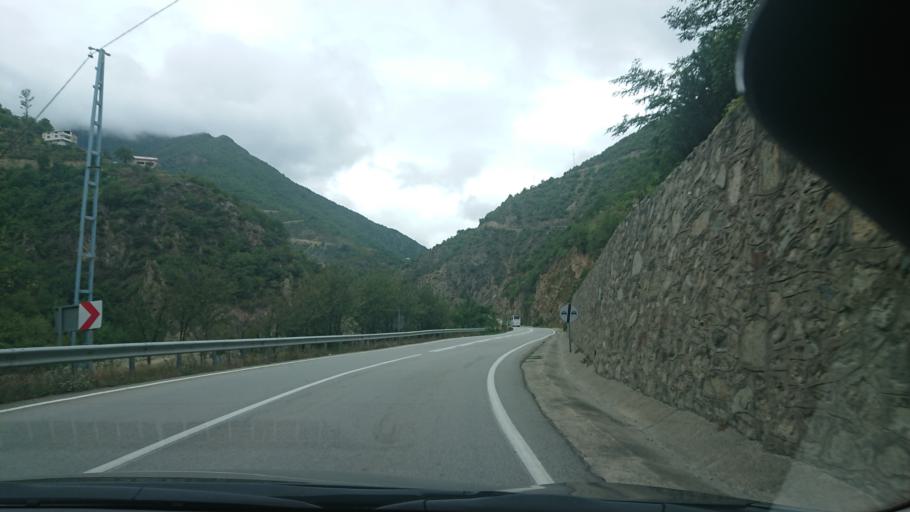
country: TR
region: Gumushane
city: Kurtun
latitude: 40.7031
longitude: 39.0756
